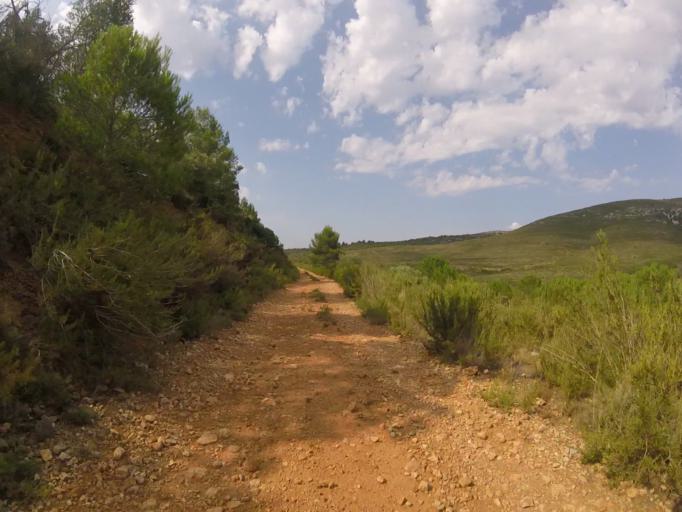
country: ES
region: Valencia
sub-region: Provincia de Castello
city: Alcala de Xivert
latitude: 40.3495
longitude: 0.1990
